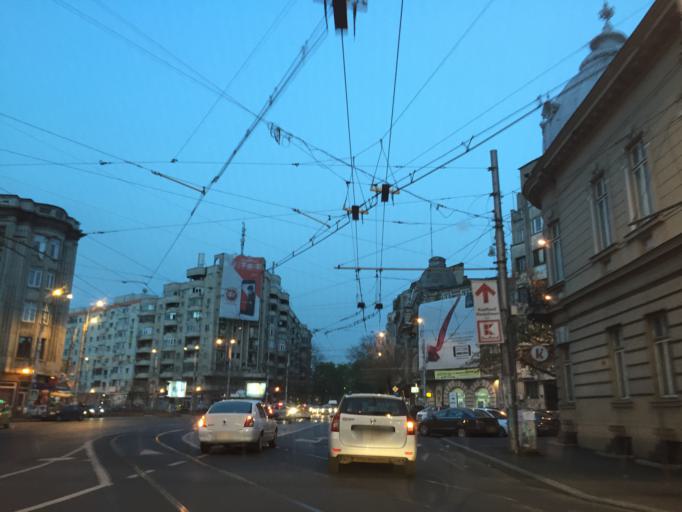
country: RO
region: Bucuresti
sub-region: Municipiul Bucuresti
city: Bucharest
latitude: 44.4376
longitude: 26.1135
